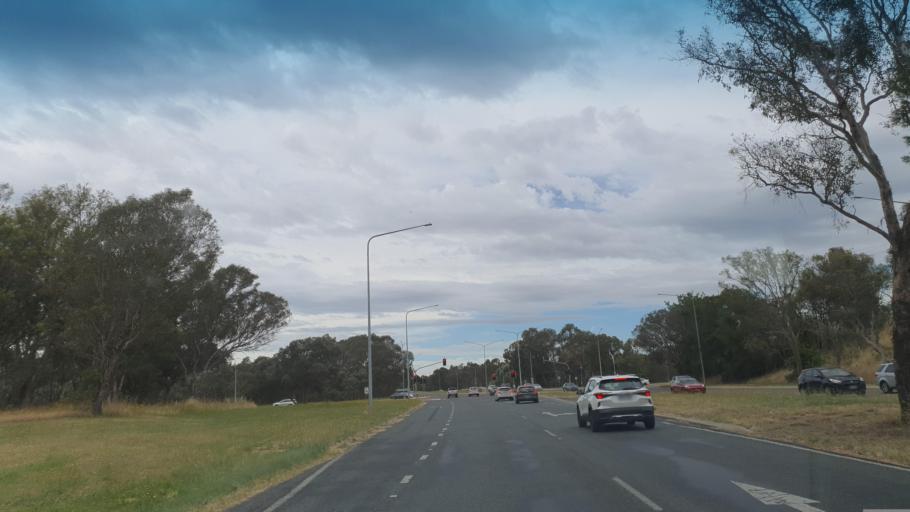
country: AU
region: Australian Capital Territory
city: Macquarie
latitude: -35.2167
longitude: 149.0422
